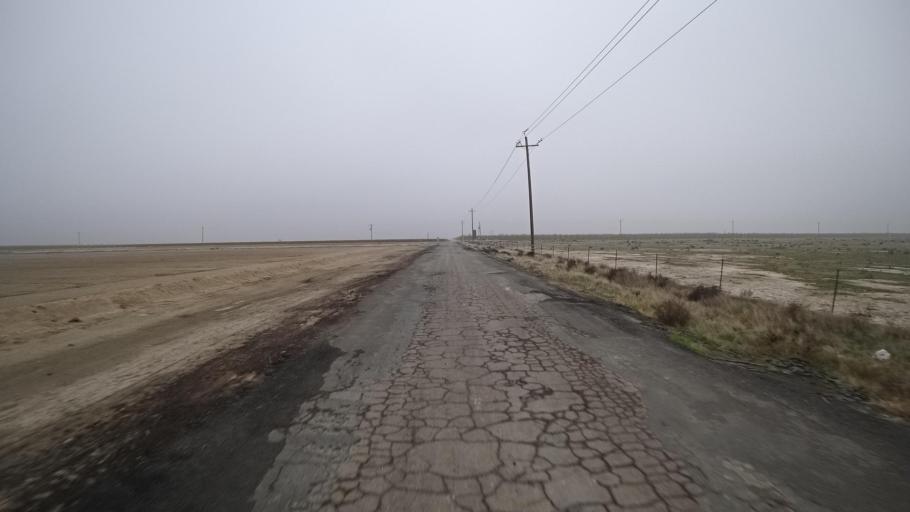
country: US
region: California
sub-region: Tulare County
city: Alpaugh
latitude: 35.7630
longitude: -119.4013
